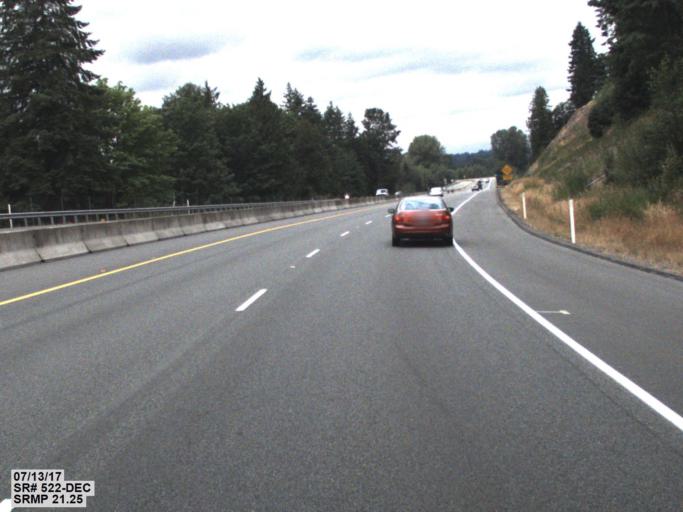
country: US
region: Washington
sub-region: Snohomish County
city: Cathcart
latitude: 47.8296
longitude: -122.0346
